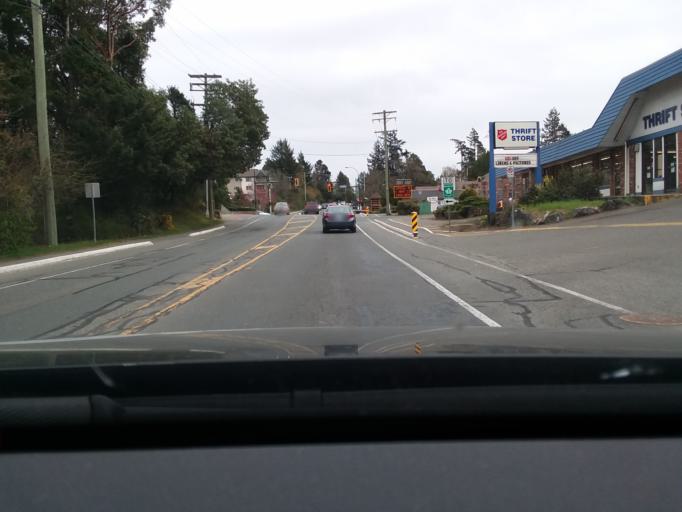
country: CA
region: British Columbia
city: Colwood
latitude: 48.4567
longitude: -123.4424
